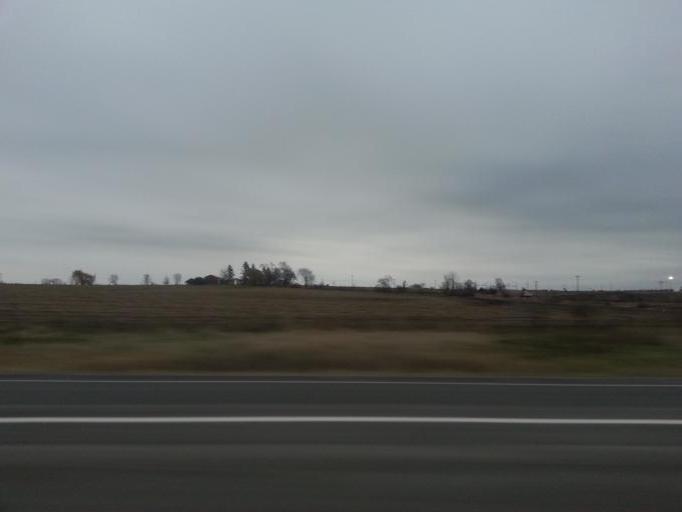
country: US
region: Iowa
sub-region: Linn County
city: Robins
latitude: 42.0958
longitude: -91.7014
